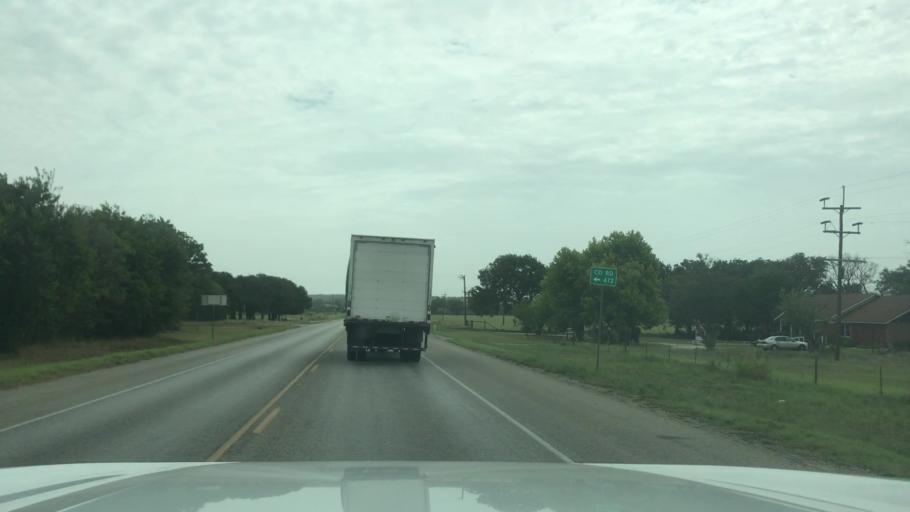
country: US
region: Texas
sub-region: Comanche County
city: De Leon
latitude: 32.0966
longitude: -98.4606
